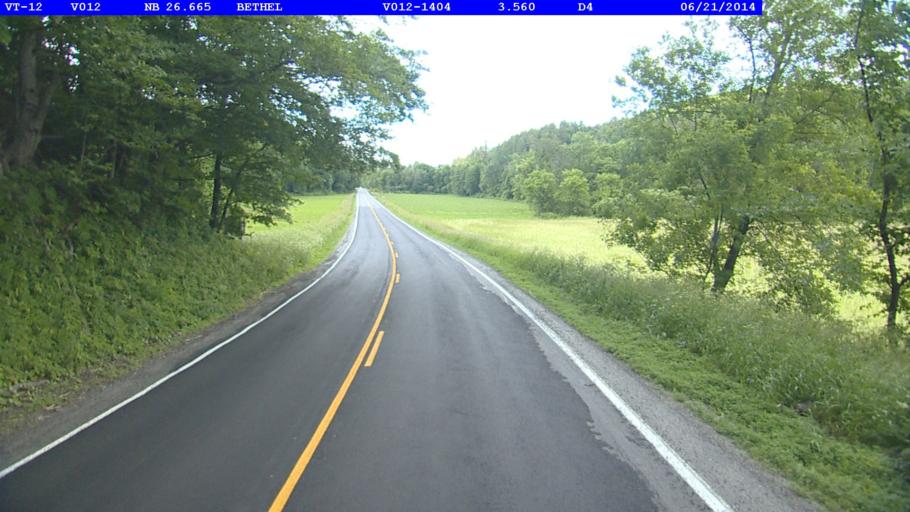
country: US
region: Vermont
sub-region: Orange County
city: Randolph
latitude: 43.8490
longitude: -72.6472
